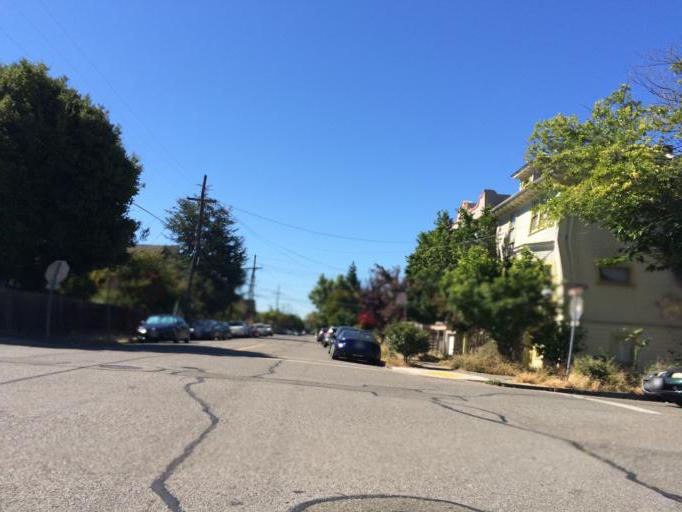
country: US
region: California
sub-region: Alameda County
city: Berkeley
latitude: 37.8623
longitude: -122.2742
